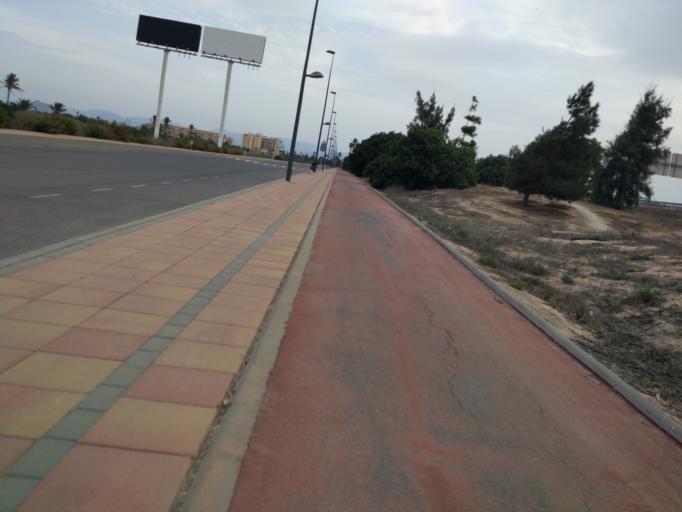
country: ES
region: Murcia
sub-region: Murcia
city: Los Alcazares
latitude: 37.7362
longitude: -0.8715
